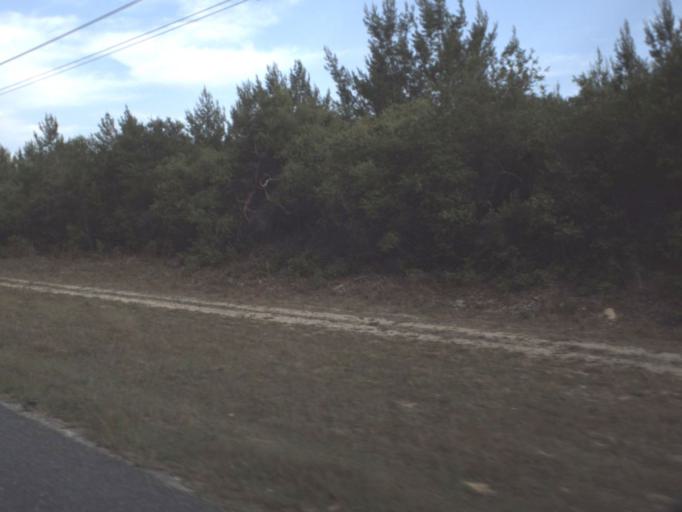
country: US
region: Florida
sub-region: Lake County
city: Astor
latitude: 29.1776
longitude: -81.7491
